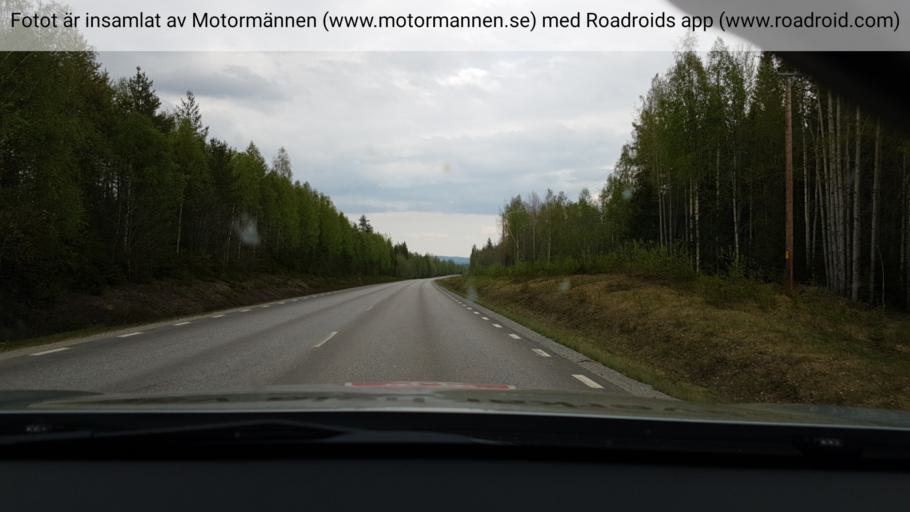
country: SE
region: Vaesterbotten
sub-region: Vannas Kommun
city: Vaennaes
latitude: 63.9257
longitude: 19.5844
